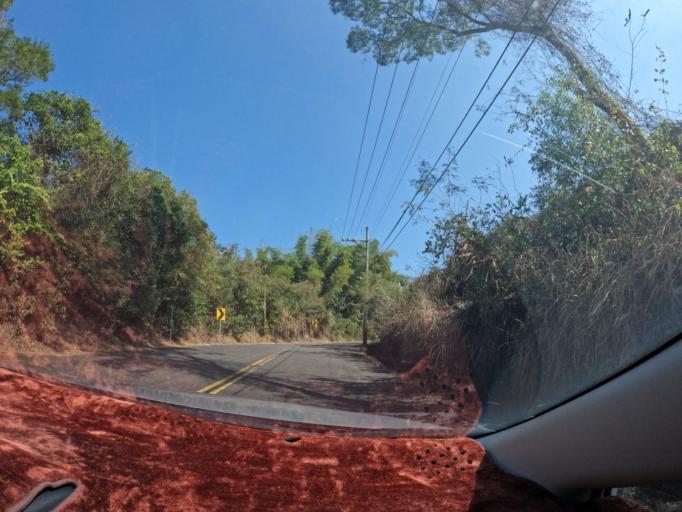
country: TW
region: Taiwan
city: Yujing
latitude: 23.0357
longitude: 120.3569
